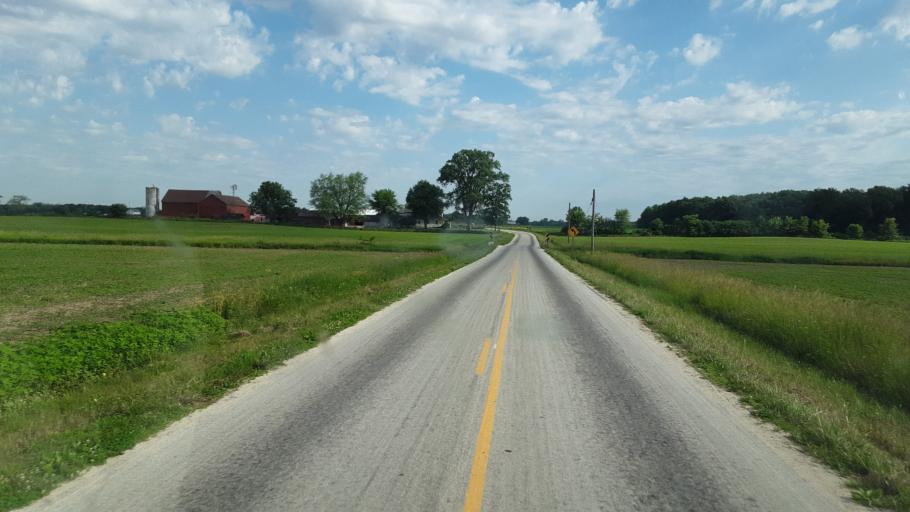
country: US
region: Ohio
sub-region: Hardin County
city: Kenton
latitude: 40.5955
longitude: -83.4644
